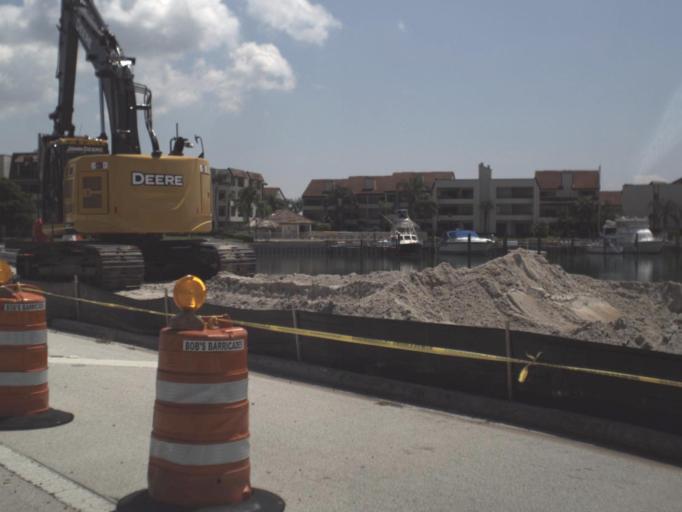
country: US
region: Florida
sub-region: Pinellas County
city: Tierra Verde
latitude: 27.6890
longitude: -82.7206
